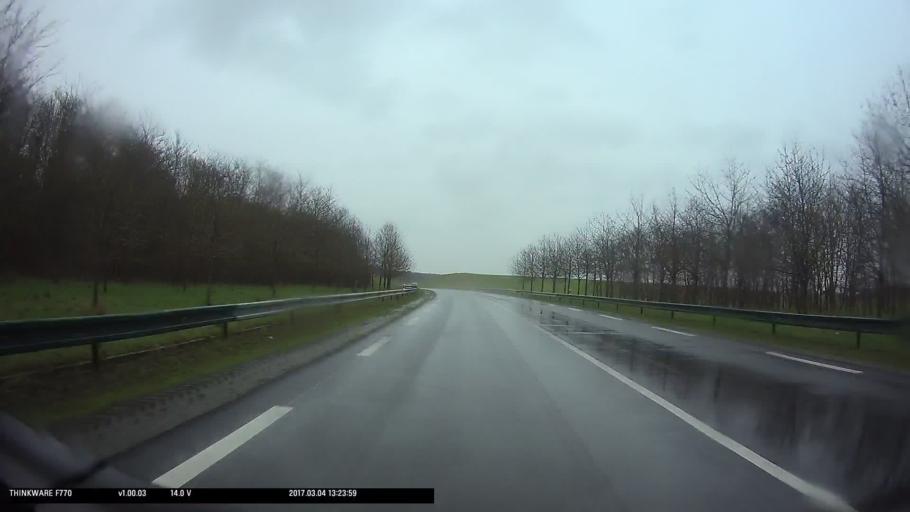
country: FR
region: Ile-de-France
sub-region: Departement du Val-d'Oise
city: Marines
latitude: 49.1361
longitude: 1.9726
